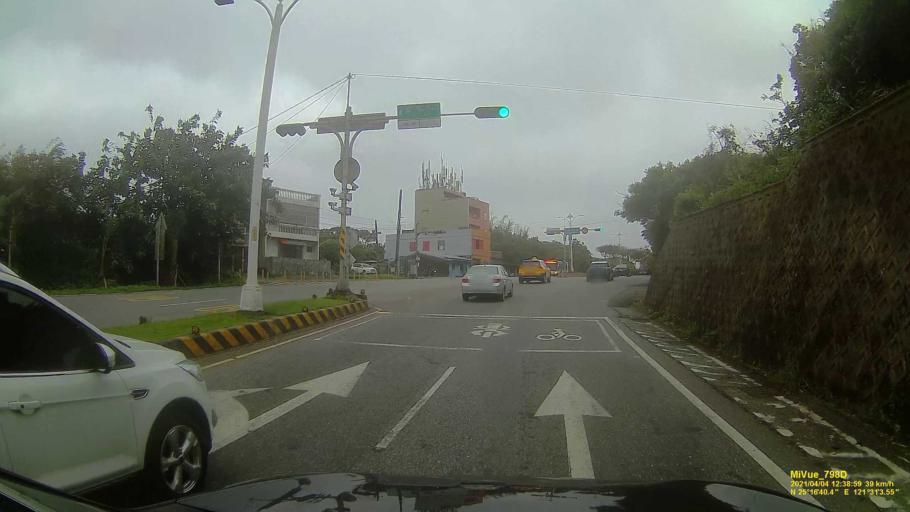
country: TW
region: Taipei
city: Taipei
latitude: 25.2777
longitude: 121.5175
